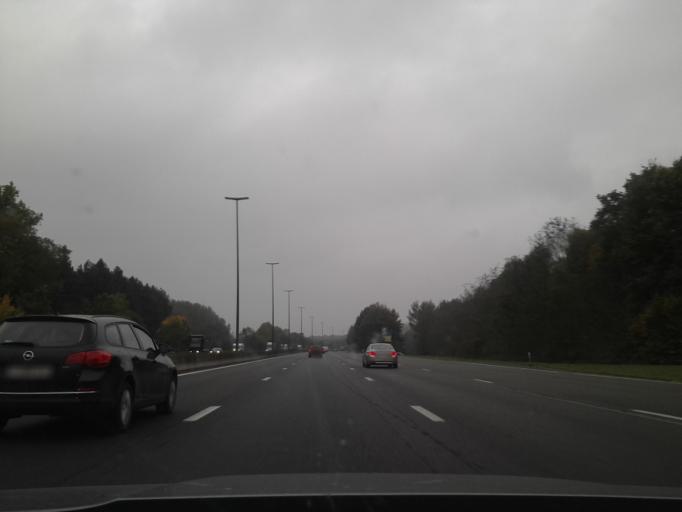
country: BE
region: Wallonia
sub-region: Province du Hainaut
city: Mons
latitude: 50.4892
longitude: 3.9784
